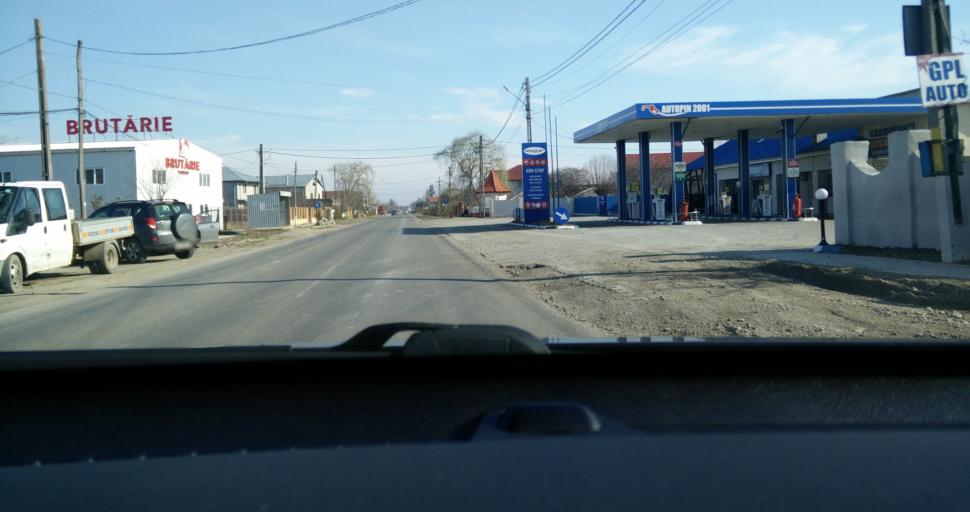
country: RO
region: Vrancea
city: Vulturu de Sus
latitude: 45.6236
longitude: 27.4017
